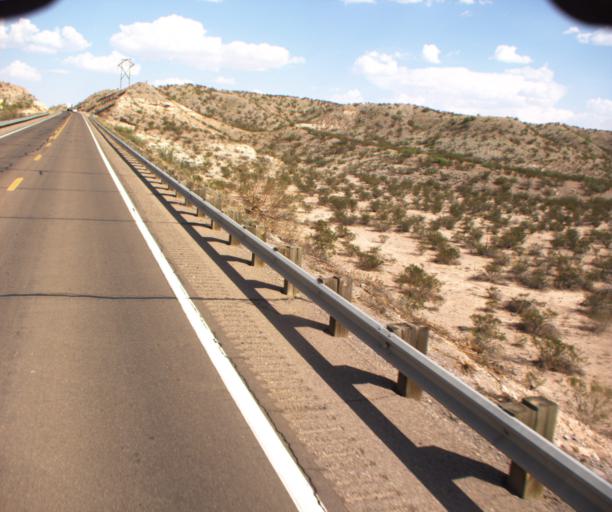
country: US
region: Arizona
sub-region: Greenlee County
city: Clifton
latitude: 32.7583
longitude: -109.1358
